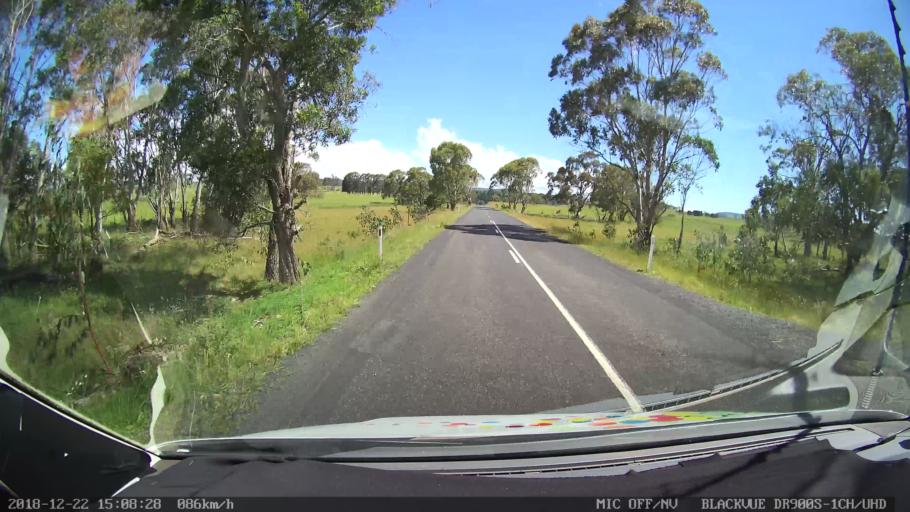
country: AU
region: New South Wales
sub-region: Bellingen
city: Dorrigo
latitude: -30.3128
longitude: 152.4136
